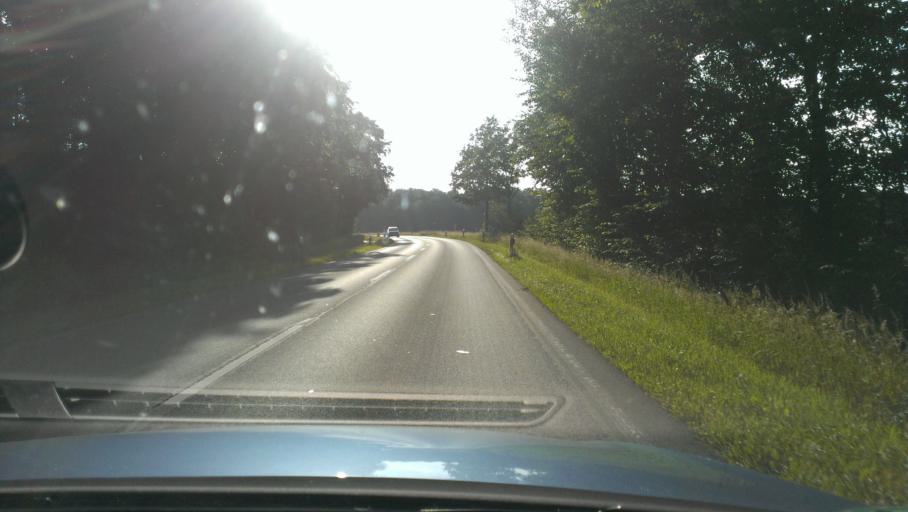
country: DE
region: North Rhine-Westphalia
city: Sendenhorst
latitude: 51.8561
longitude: 7.7815
